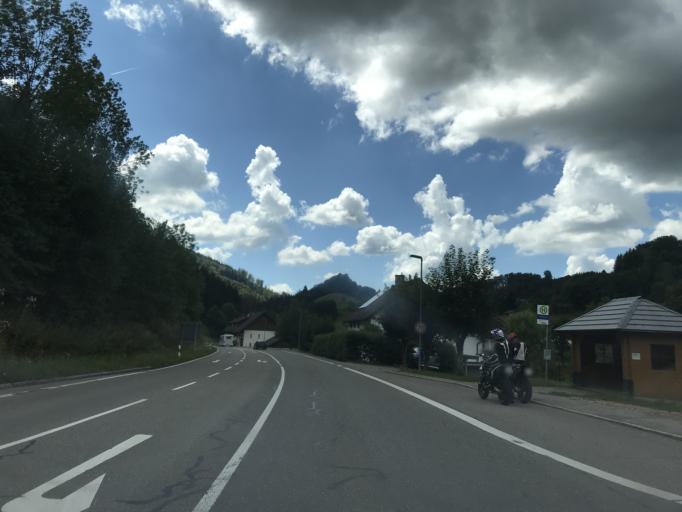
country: DE
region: Baden-Wuerttemberg
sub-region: Freiburg Region
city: Wembach
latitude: 47.7608
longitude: 7.8856
